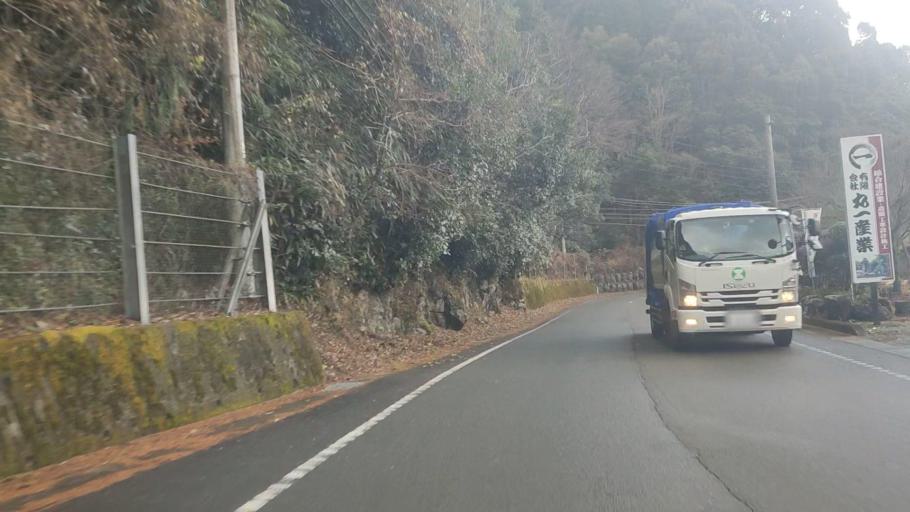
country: JP
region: Kumamoto
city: Hitoyoshi
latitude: 32.4327
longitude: 130.8610
